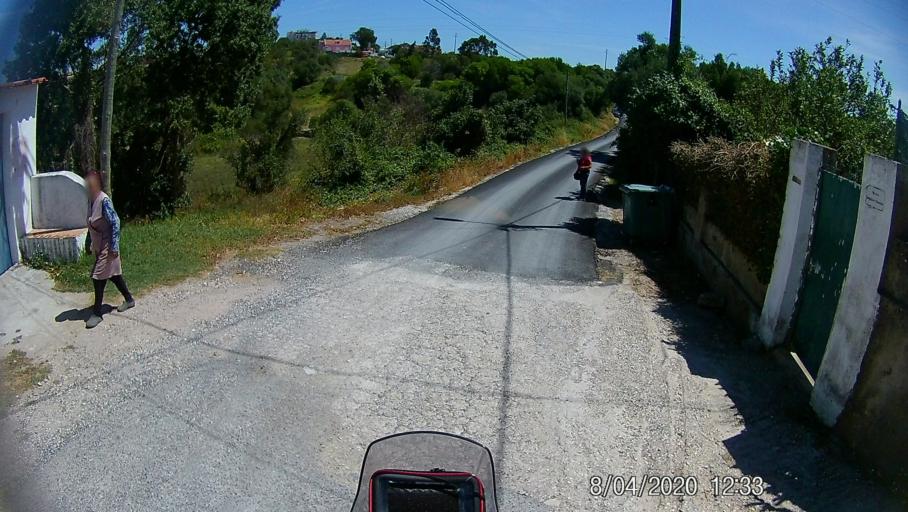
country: PT
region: Lisbon
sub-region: Sintra
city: Rio de Mouro
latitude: 38.7530
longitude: -9.3628
